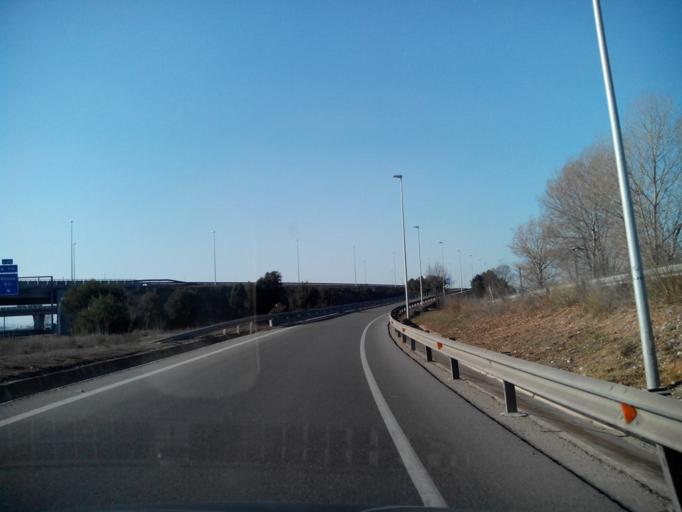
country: ES
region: Catalonia
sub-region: Provincia de Barcelona
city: Navarcles
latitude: 41.7813
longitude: 1.8895
